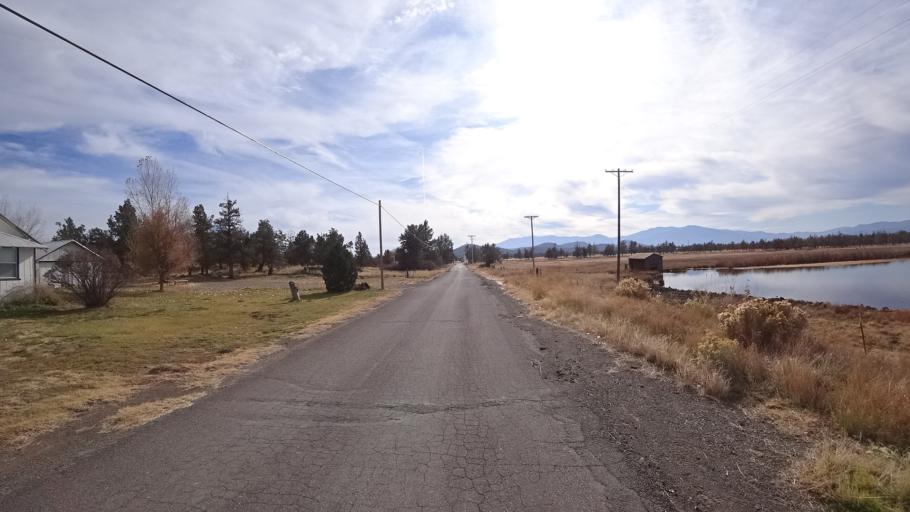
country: US
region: California
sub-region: Siskiyou County
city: Weed
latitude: 41.5982
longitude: -122.4033
